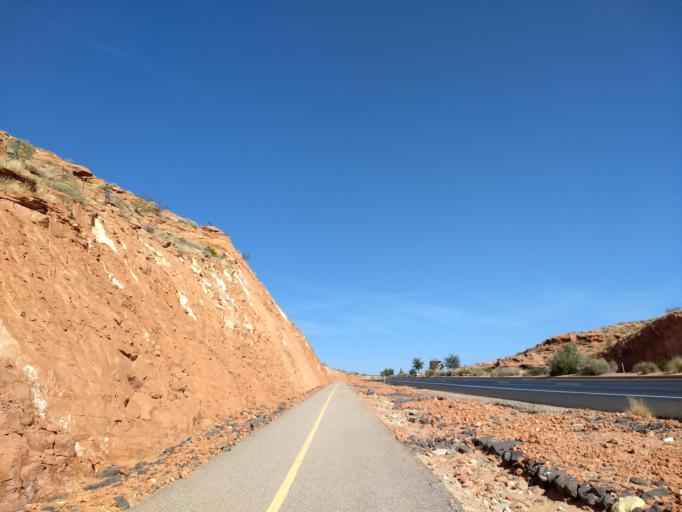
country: US
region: Utah
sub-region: Washington County
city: Saint George
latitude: 37.1208
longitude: -113.5837
